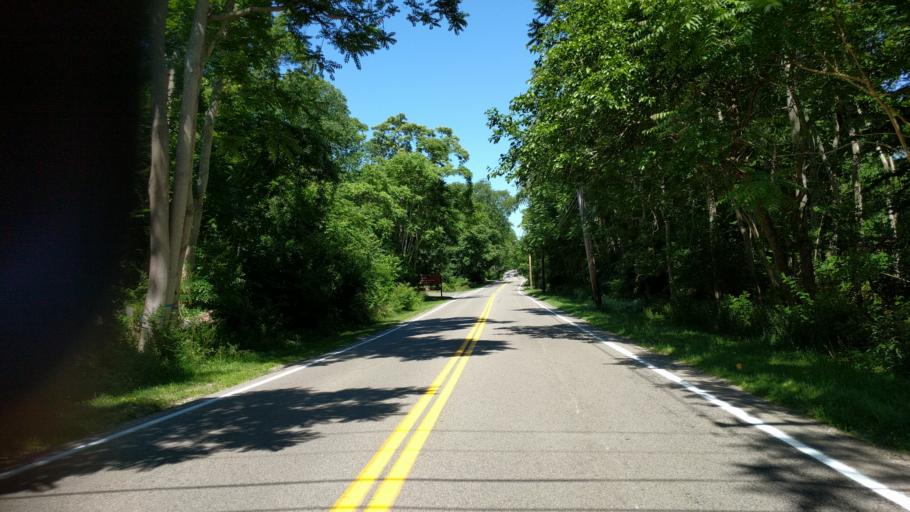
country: US
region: New York
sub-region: Suffolk County
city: Noyack
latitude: 40.9862
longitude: -72.3703
